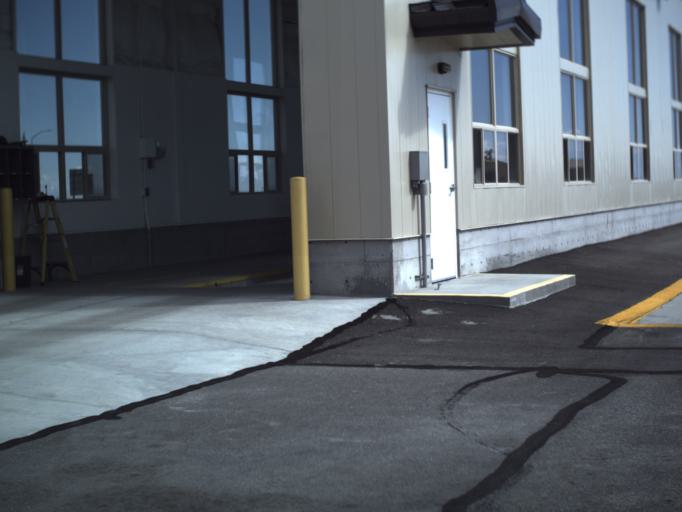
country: US
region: Utah
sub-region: Tooele County
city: Wendover
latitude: 40.7444
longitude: -113.9902
